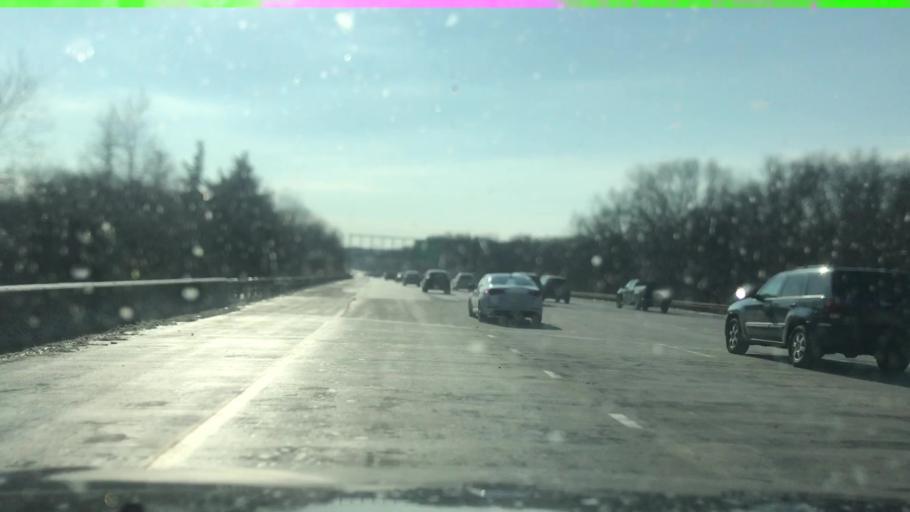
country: US
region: New Jersey
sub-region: Monmouth County
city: Shark River Hills
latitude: 40.1946
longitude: -74.1004
